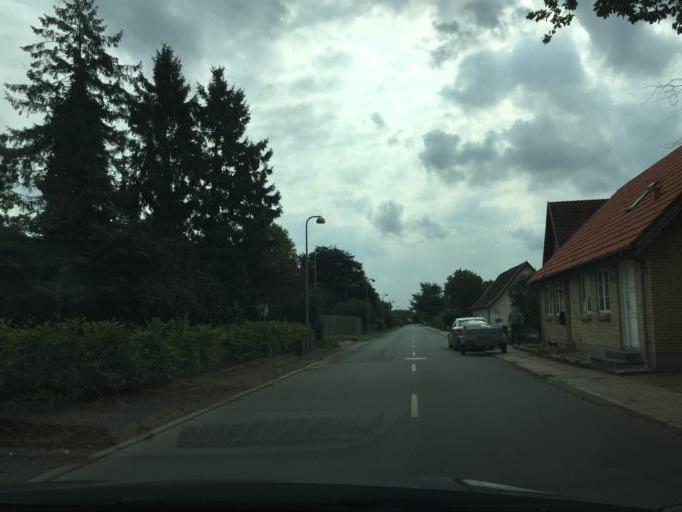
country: DK
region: South Denmark
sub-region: Odense Kommune
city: Stige
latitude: 55.4404
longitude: 10.4091
